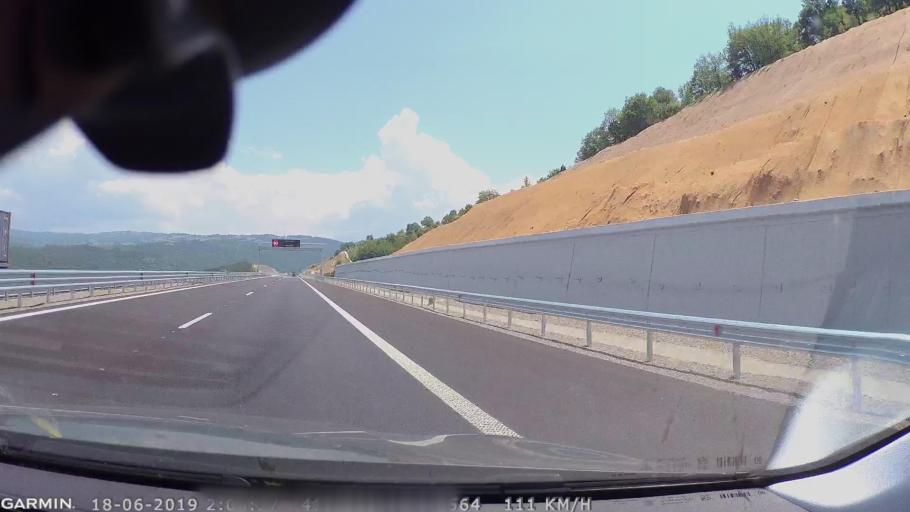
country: BG
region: Blagoevgrad
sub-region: Obshtina Blagoevgrad
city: Blagoevgrad
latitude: 41.9741
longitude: 23.0765
